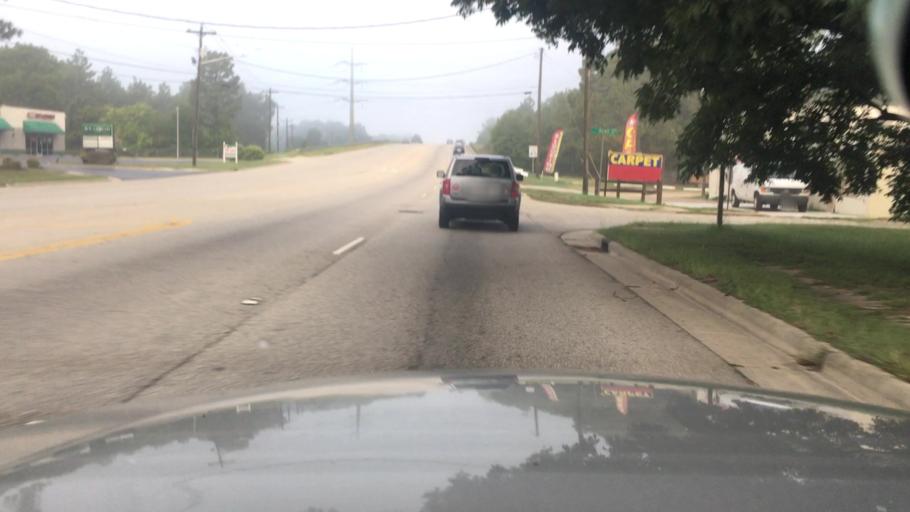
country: US
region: North Carolina
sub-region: Cumberland County
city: Fayetteville
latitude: 35.0181
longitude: -78.9198
